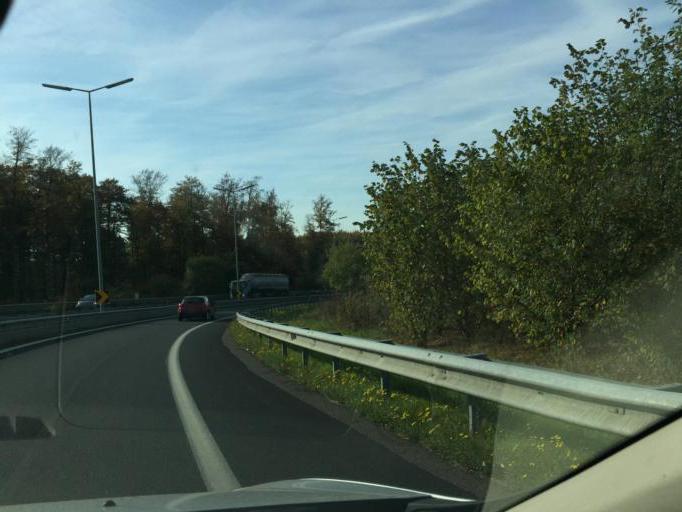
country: LU
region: Luxembourg
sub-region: Canton de Luxembourg
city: Sandweiler
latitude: 49.6398
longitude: 6.1915
